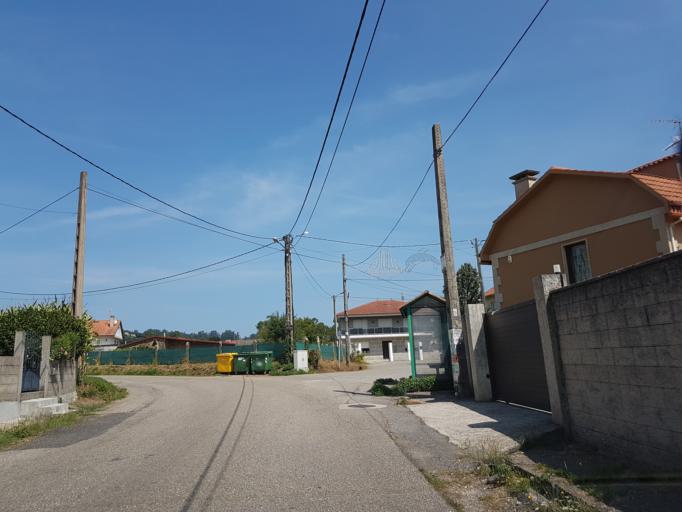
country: ES
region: Galicia
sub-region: Provincia de Pontevedra
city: Porrino
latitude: 42.2104
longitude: -8.6192
